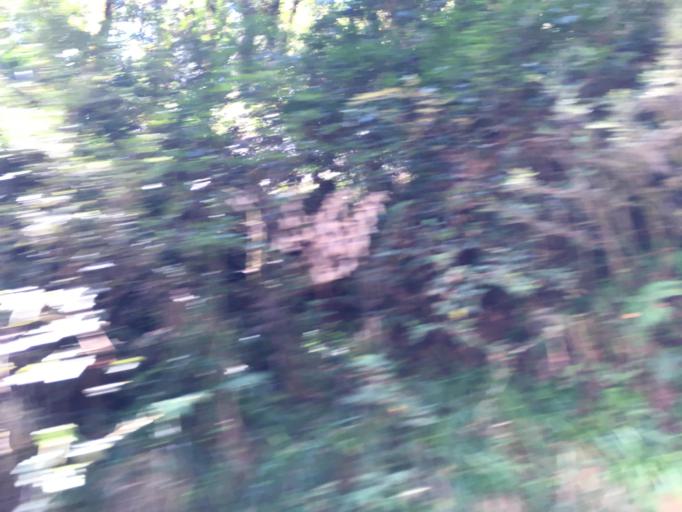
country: TW
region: Taiwan
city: Daxi
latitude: 24.5512
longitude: 121.3975
